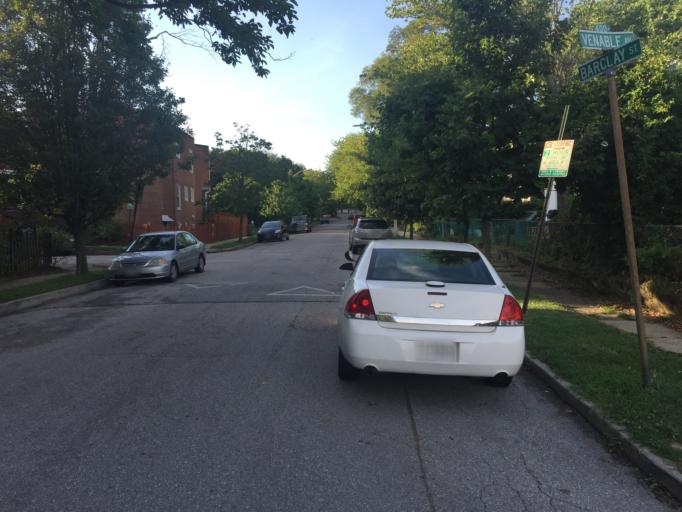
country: US
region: Maryland
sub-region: City of Baltimore
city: Baltimore
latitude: 39.3293
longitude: -76.6111
